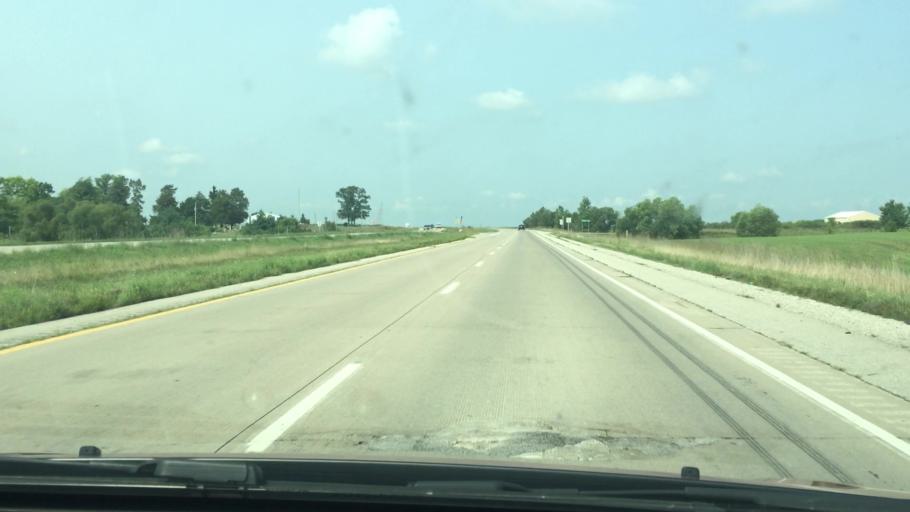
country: US
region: Iowa
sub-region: Scott County
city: Blue Grass
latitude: 41.5190
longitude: -90.8533
